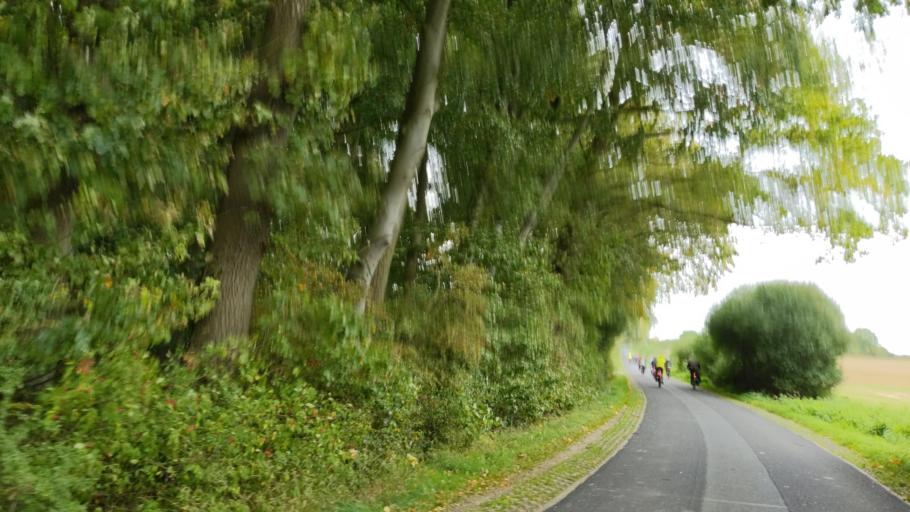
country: DE
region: Schleswig-Holstein
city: Romnitz
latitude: 53.7310
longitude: 10.7740
